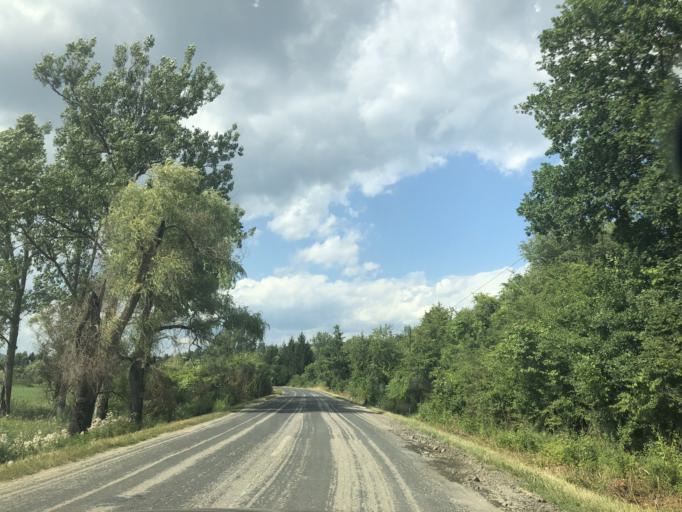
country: HU
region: Borsod-Abauj-Zemplen
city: Szendro
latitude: 48.4523
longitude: 20.7969
